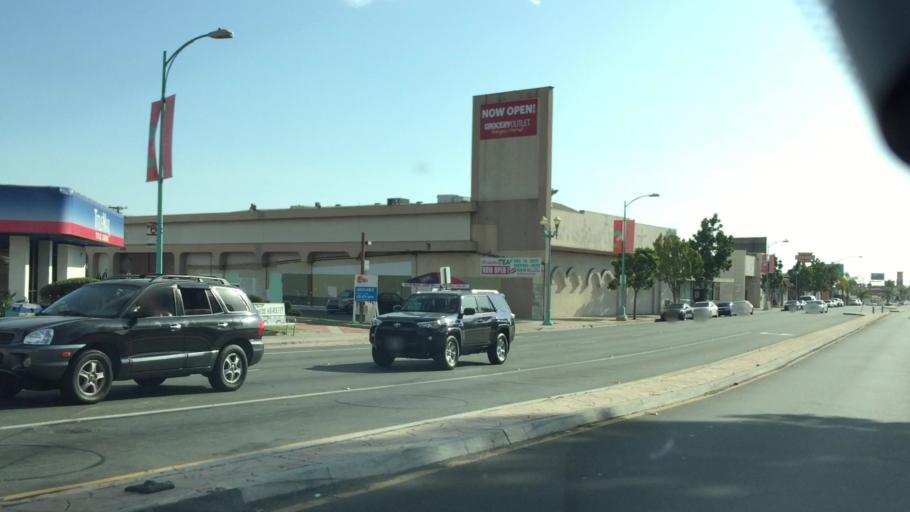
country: US
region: California
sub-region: San Diego County
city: Lemon Grove
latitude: 32.7579
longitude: -117.0796
